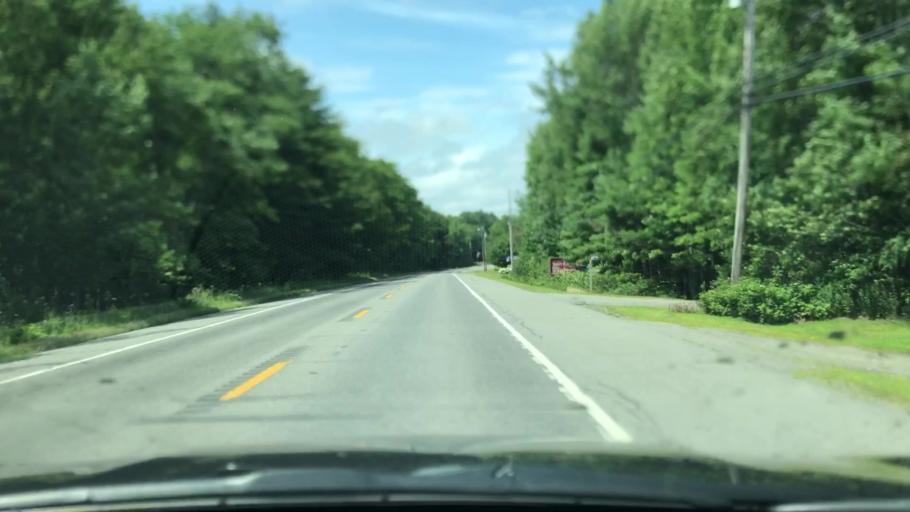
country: US
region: Maine
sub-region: Waldo County
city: Northport
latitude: 44.3699
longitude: -68.9820
